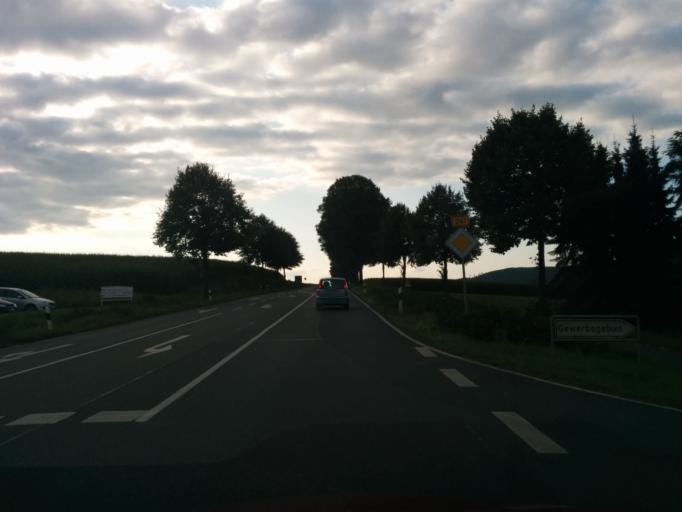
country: DE
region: Lower Saxony
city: Katlenburg-Lindau
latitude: 51.6873
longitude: 10.0949
